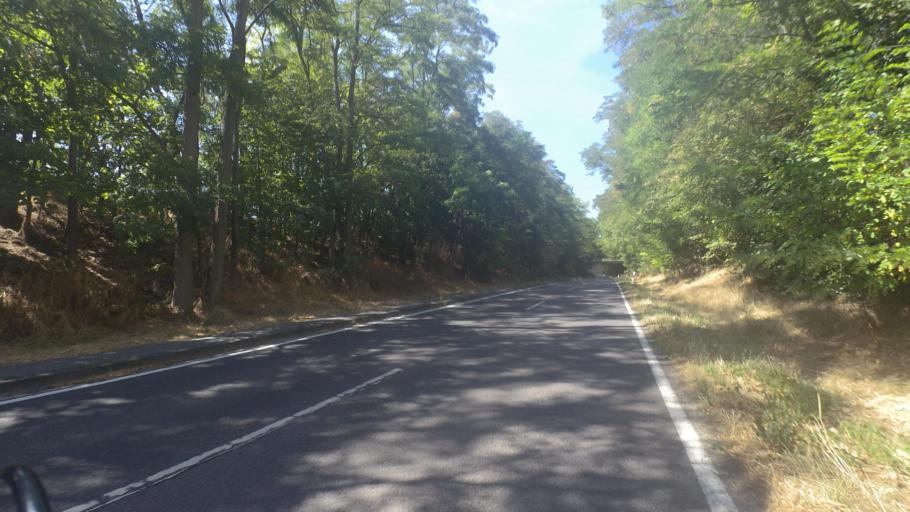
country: DE
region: Rheinland-Pfalz
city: Udenheim
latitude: 49.8691
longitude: 8.1650
